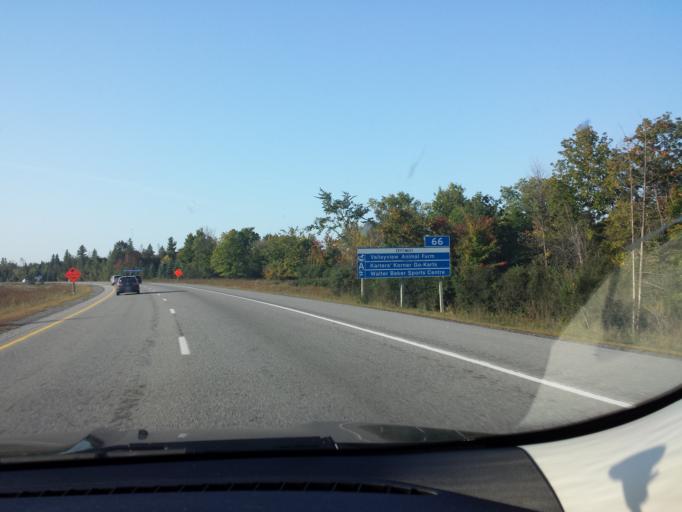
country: CA
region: Ontario
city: Bells Corners
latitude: 45.2884
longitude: -75.8045
